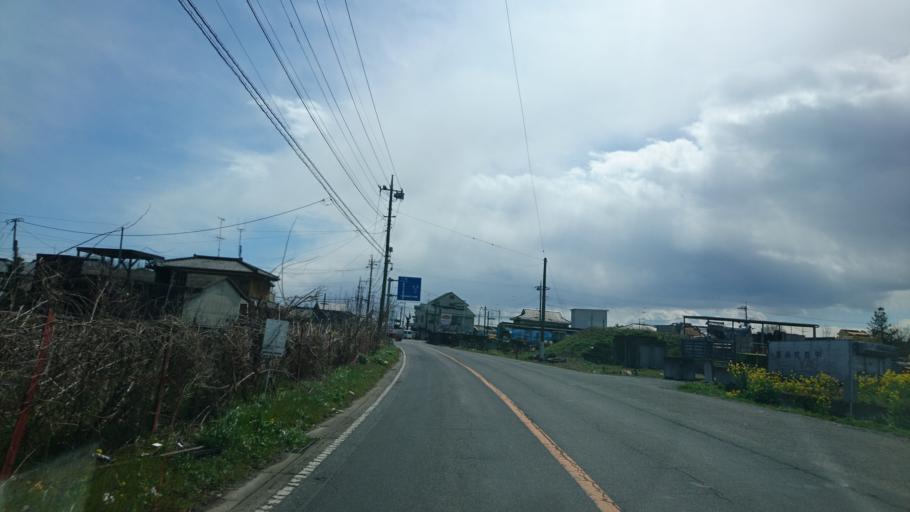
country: JP
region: Ibaraki
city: Yuki
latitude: 36.2767
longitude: 139.9121
